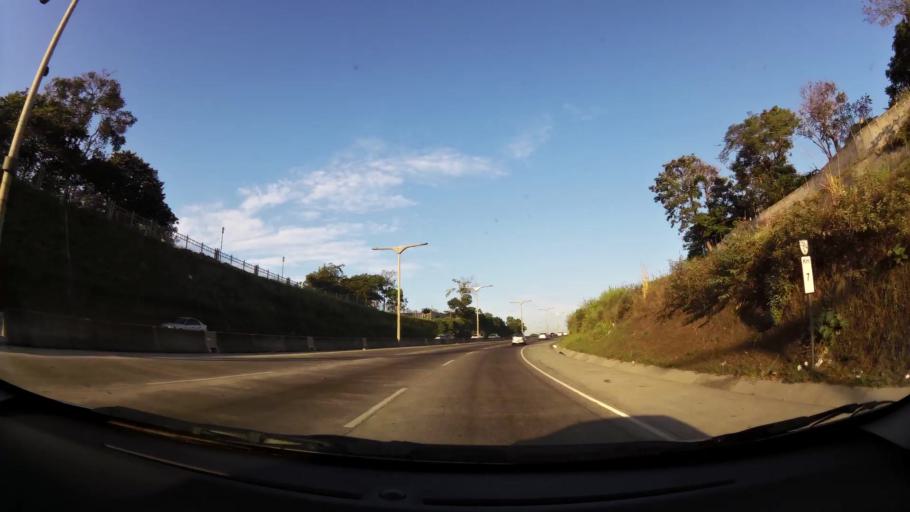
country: SV
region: La Libertad
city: Antiguo Cuscatlan
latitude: 13.6842
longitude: -89.2471
